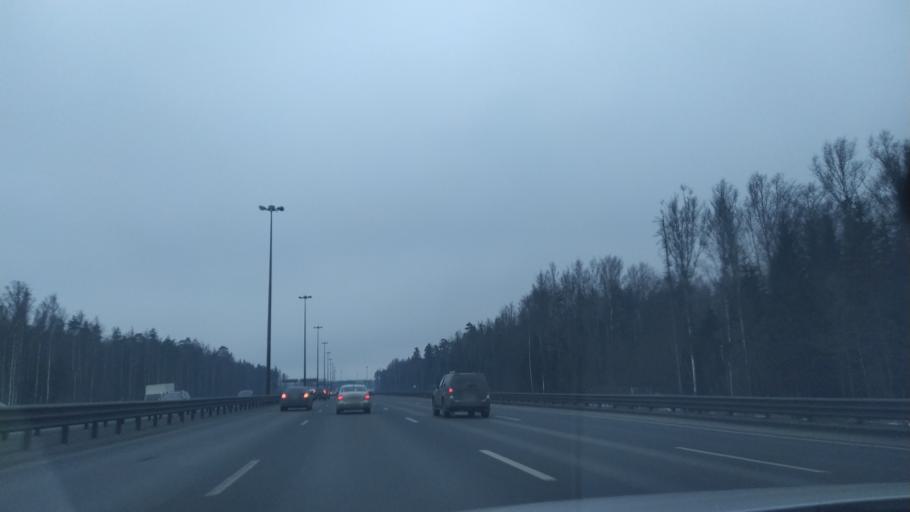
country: RU
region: Leningrad
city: Yanino Vtoroye
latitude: 59.9552
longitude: 30.5493
